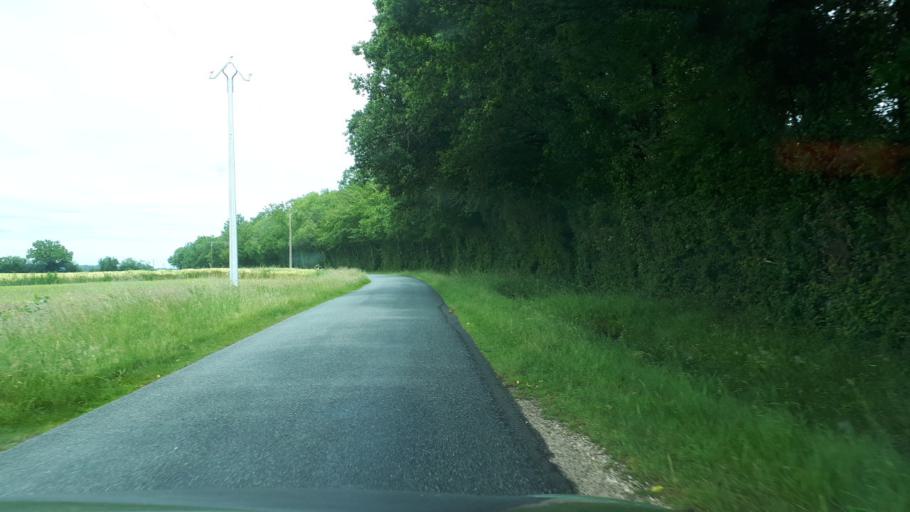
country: FR
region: Centre
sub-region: Departement du Cher
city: Henrichemont
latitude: 47.4005
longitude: 2.6498
